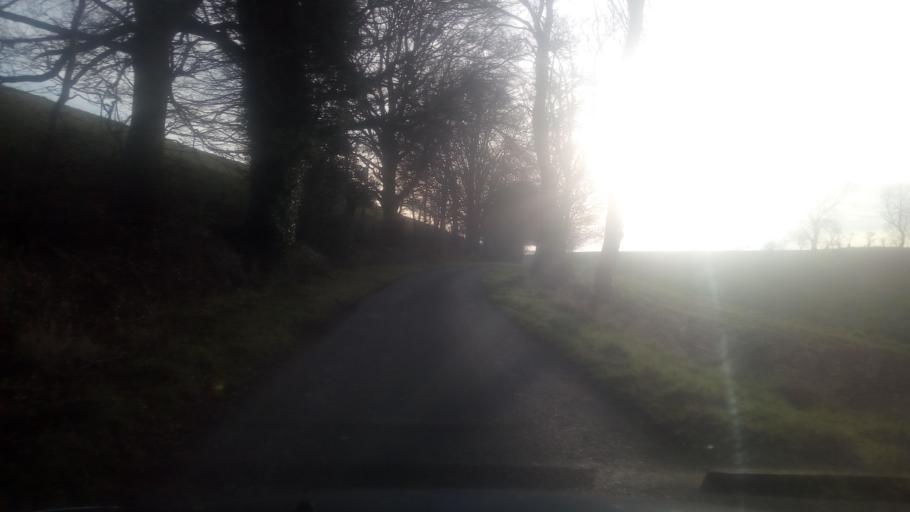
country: GB
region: Scotland
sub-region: The Scottish Borders
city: Jedburgh
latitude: 55.4653
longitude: -2.6303
